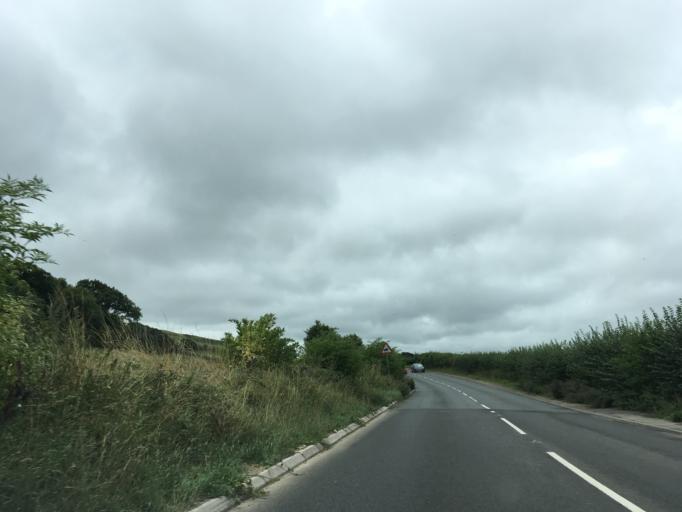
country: GB
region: England
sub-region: Bath and North East Somerset
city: Saltford
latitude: 51.3720
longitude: -2.4777
